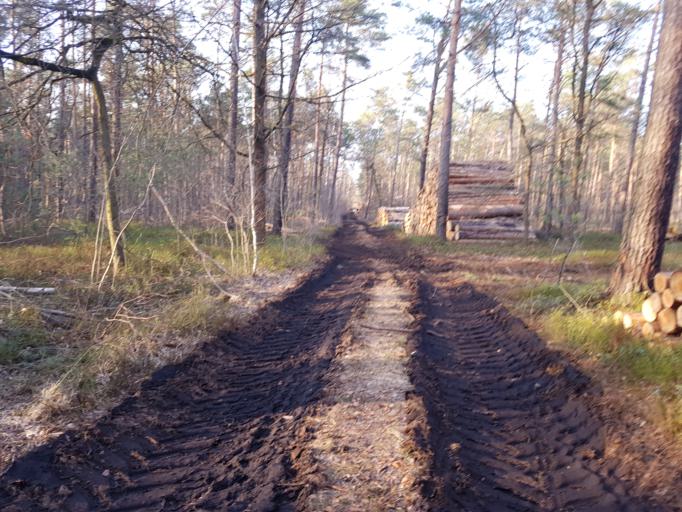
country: DE
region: Brandenburg
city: Schonewalde
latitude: 51.6313
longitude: 13.6163
